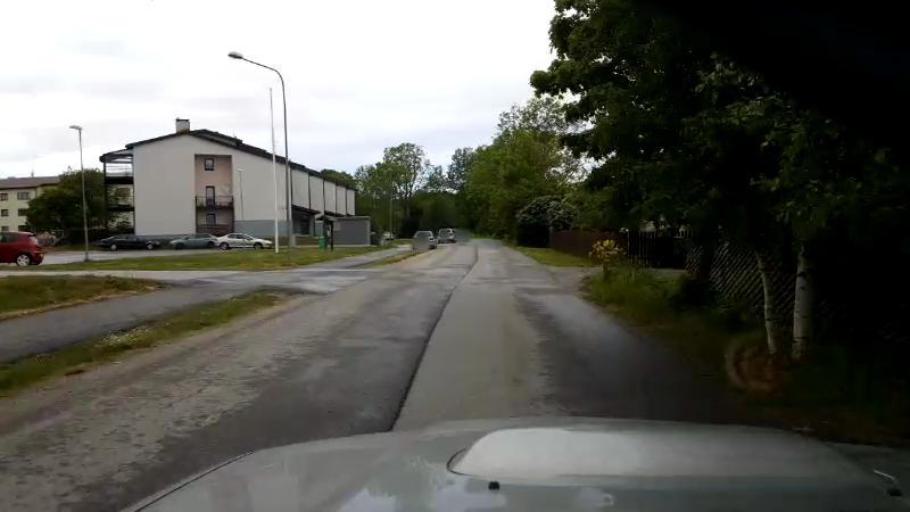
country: EE
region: Harju
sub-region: Harku vald
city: Tabasalu
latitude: 59.4562
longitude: 24.4344
